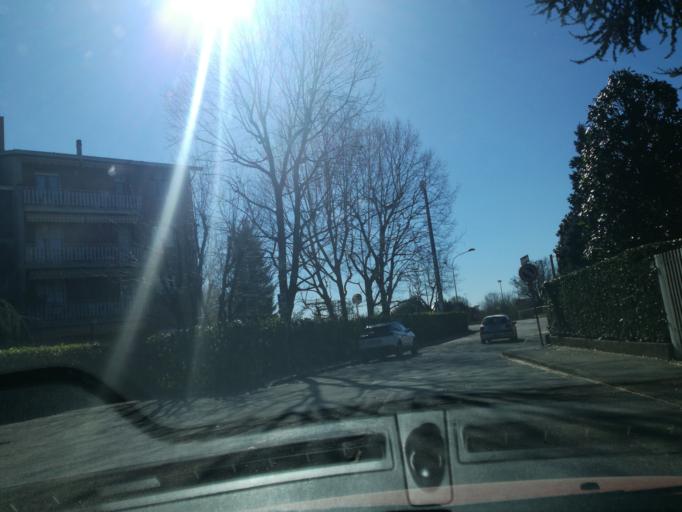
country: IT
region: Lombardy
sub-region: Provincia di Monza e Brianza
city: Vimercate
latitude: 45.6080
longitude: 9.3717
